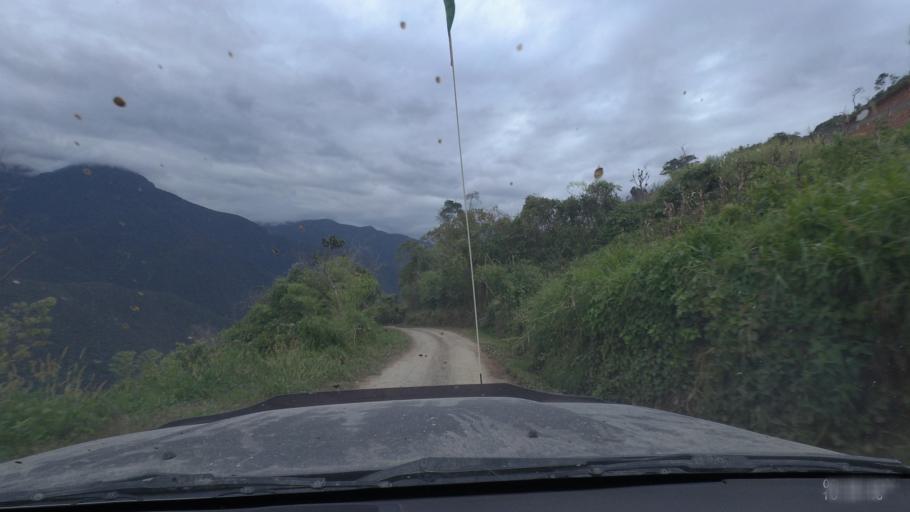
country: BO
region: La Paz
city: Quime
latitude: -16.5458
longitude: -66.7477
